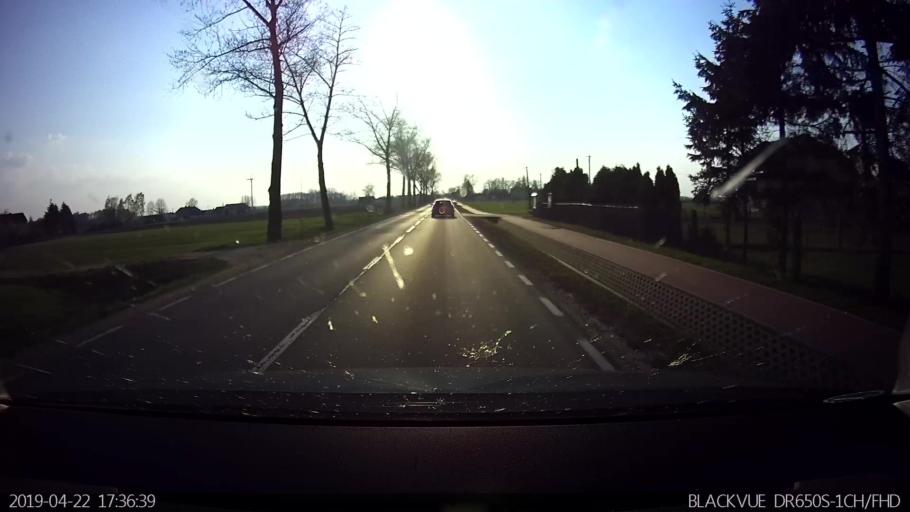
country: PL
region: Masovian Voivodeship
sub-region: Powiat sokolowski
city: Sokolow Podlaski
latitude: 52.4075
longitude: 22.1864
